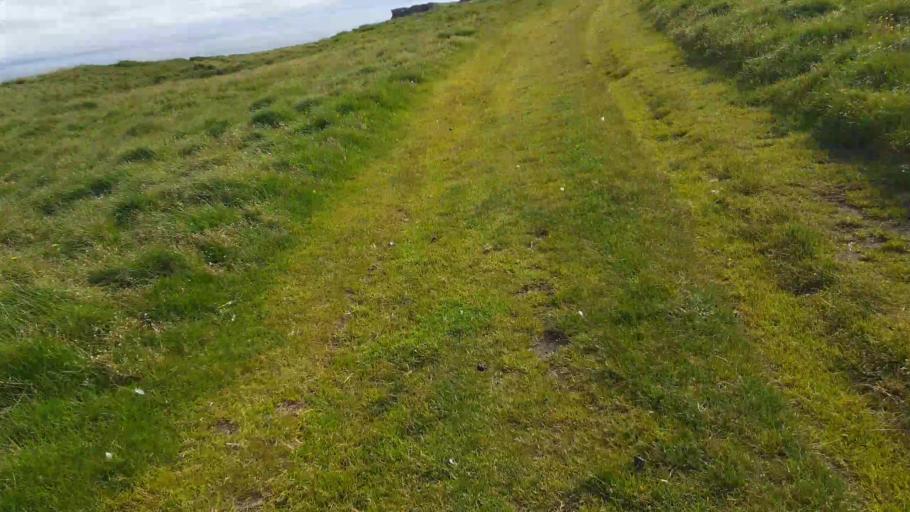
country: IS
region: Northeast
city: Dalvik
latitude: 66.5504
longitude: -17.9927
